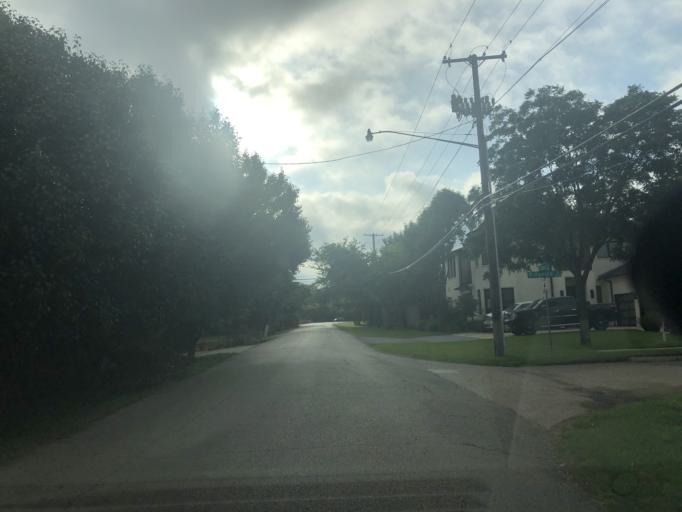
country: US
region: Texas
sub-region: Dallas County
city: University Park
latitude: 32.8560
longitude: -96.8416
